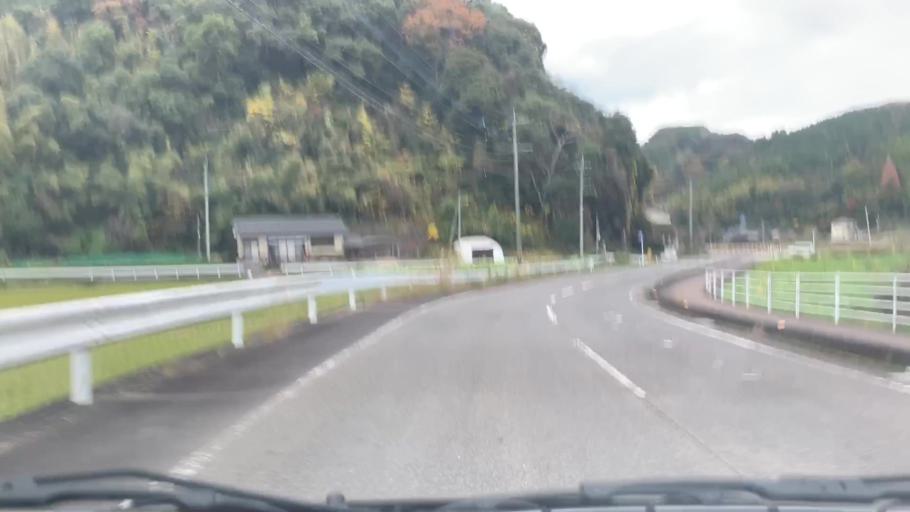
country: JP
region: Saga Prefecture
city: Kashima
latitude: 33.1014
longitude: 130.0669
